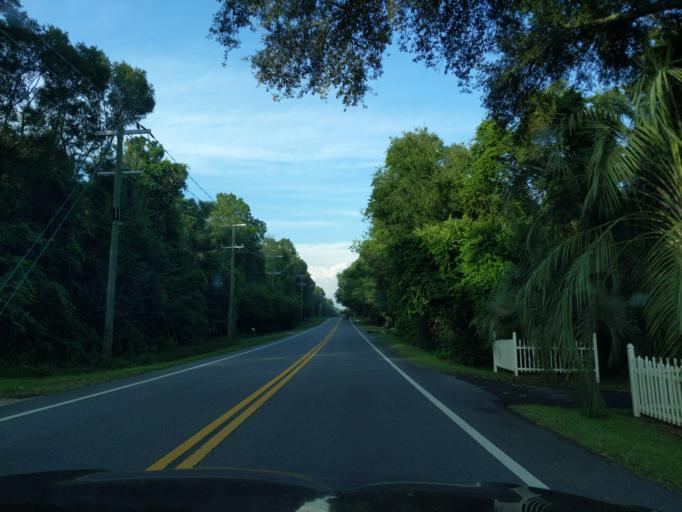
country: US
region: Florida
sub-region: Leon County
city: Tallahassee
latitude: 30.3807
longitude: -84.3469
